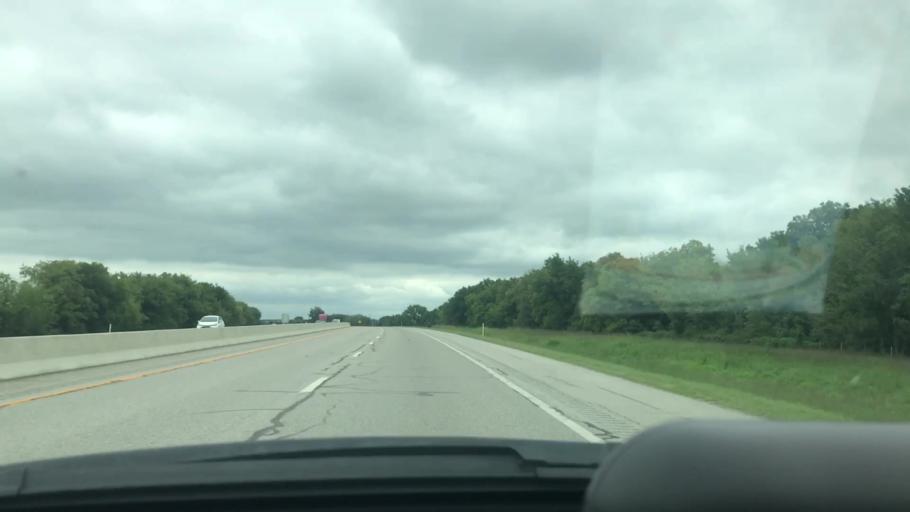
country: US
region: Oklahoma
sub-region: Ottawa County
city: Fairland
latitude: 36.7360
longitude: -94.9113
